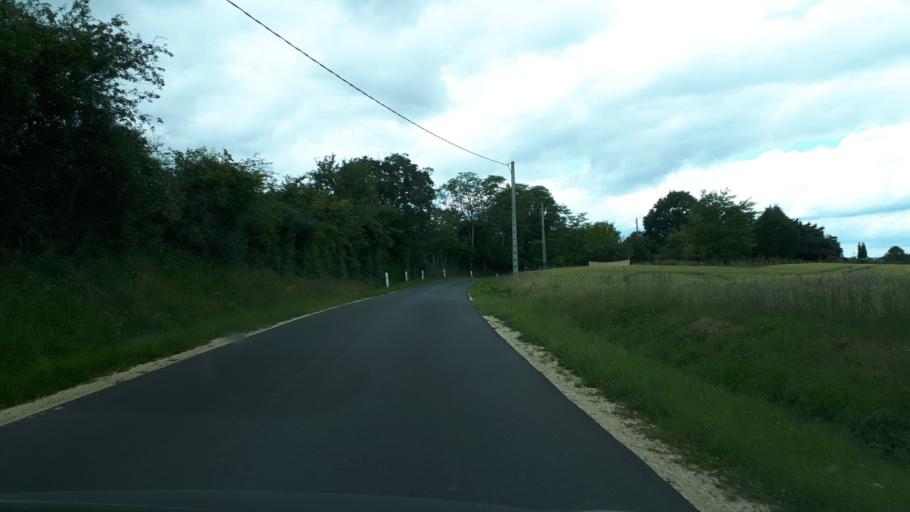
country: FR
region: Centre
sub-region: Departement du Loir-et-Cher
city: Sarge-sur-Braye
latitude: 47.9257
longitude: 0.8709
